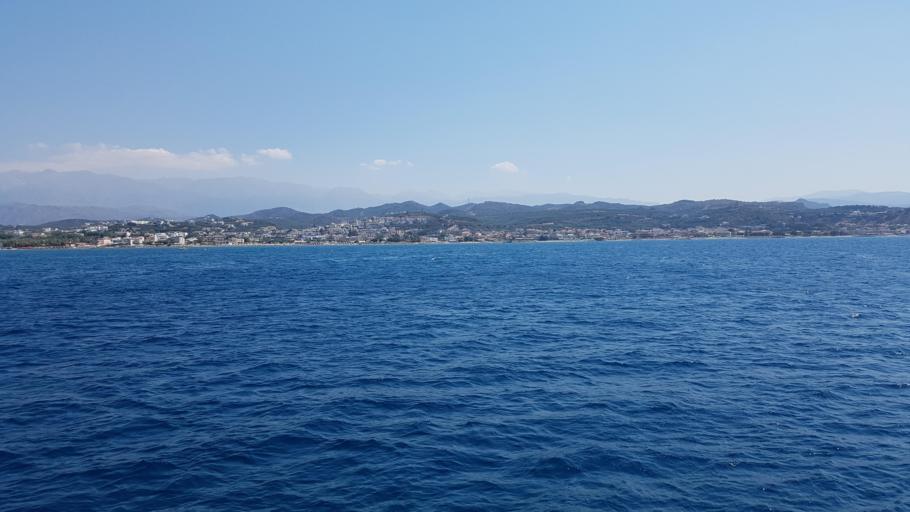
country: GR
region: Crete
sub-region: Nomos Chanias
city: Agia Marina
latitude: 35.5305
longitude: 23.9250
